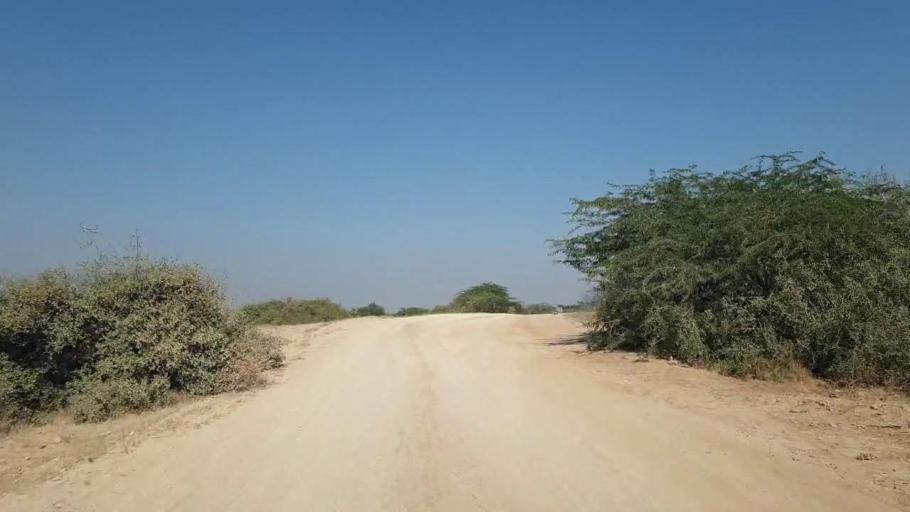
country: PK
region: Sindh
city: Jamshoro
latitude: 25.3074
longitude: 67.8174
